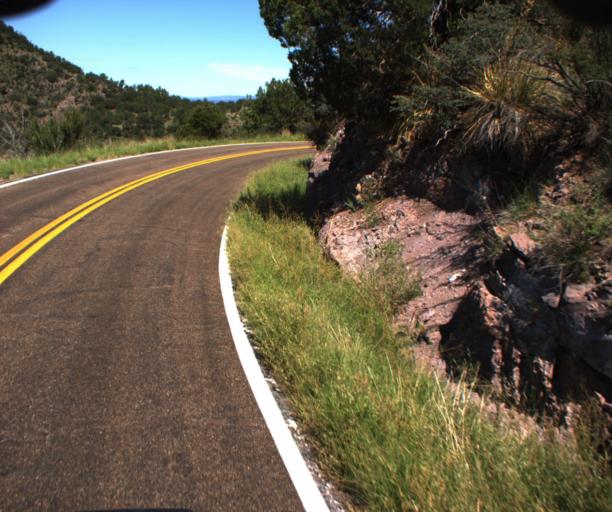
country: US
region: Arizona
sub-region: Greenlee County
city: Morenci
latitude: 33.2250
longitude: -109.3919
